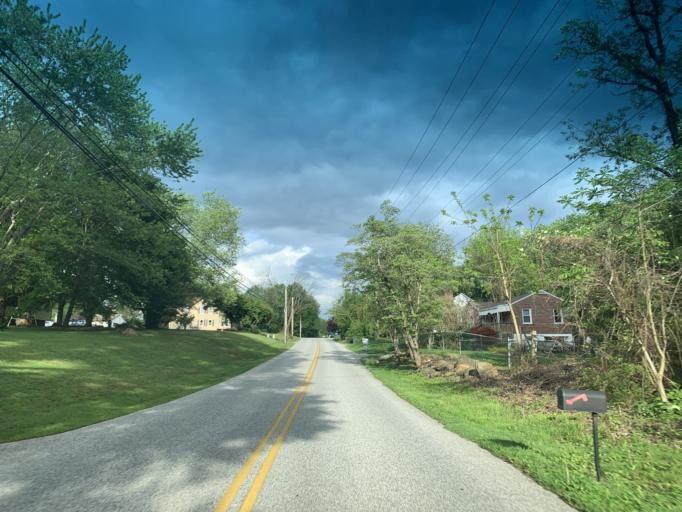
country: US
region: Maryland
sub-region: Harford County
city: South Bel Air
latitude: 39.6549
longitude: -76.2676
